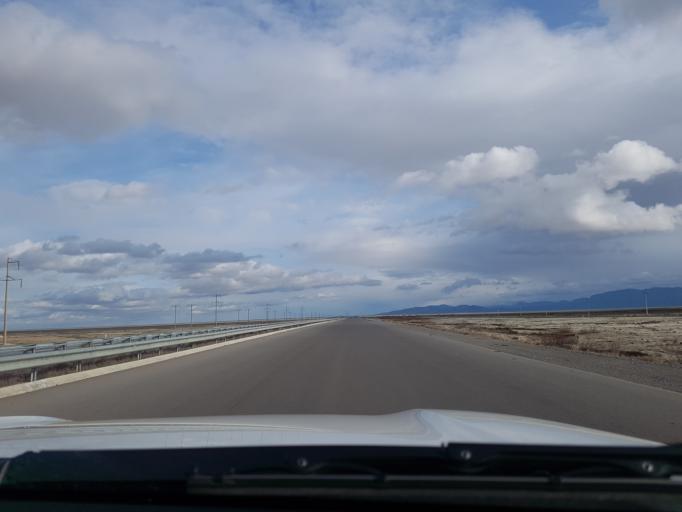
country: TM
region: Balkan
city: Serdar
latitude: 39.0870
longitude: 56.0359
